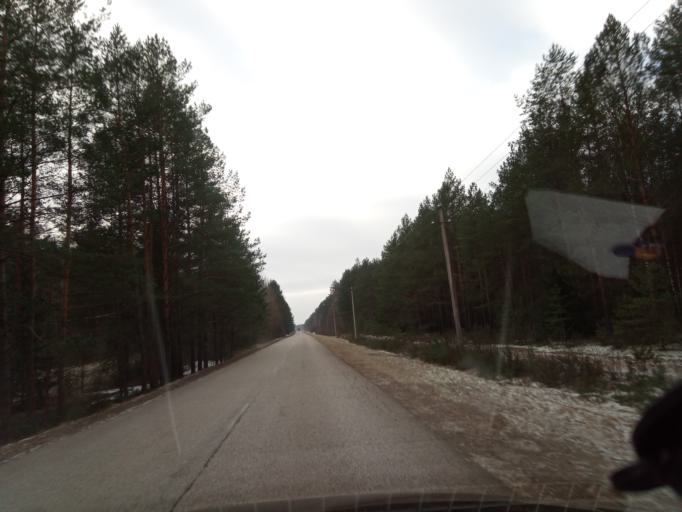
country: LT
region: Alytaus apskritis
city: Varena
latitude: 54.0348
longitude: 24.3665
